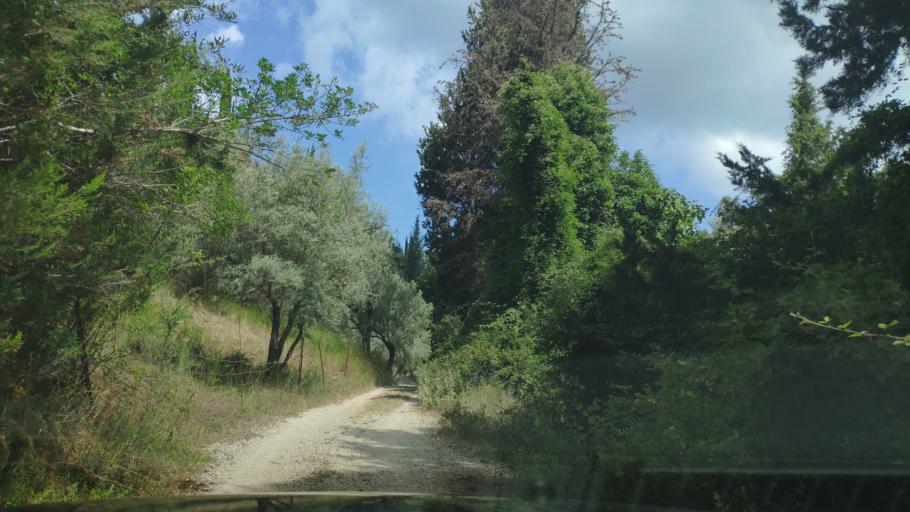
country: GR
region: Ionian Islands
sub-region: Lefkada
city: Lefkada
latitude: 38.7993
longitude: 20.6724
